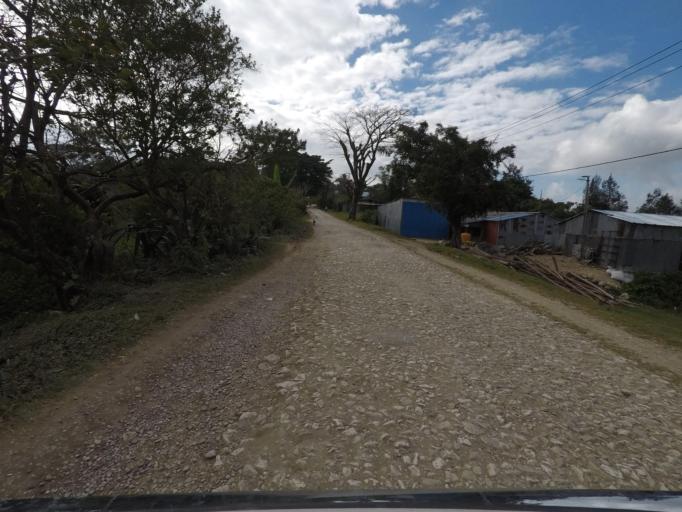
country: TL
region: Baucau
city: Venilale
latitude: -8.6401
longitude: 126.3876
